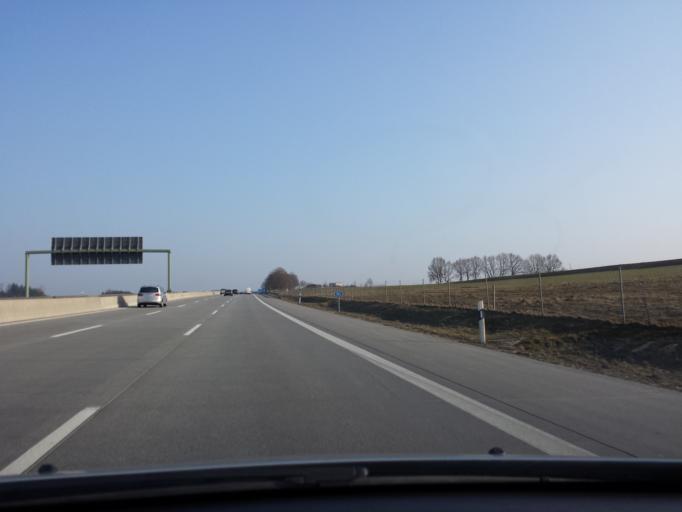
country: DE
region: Bavaria
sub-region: Swabia
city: Dasing
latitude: 48.3901
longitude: 11.0720
